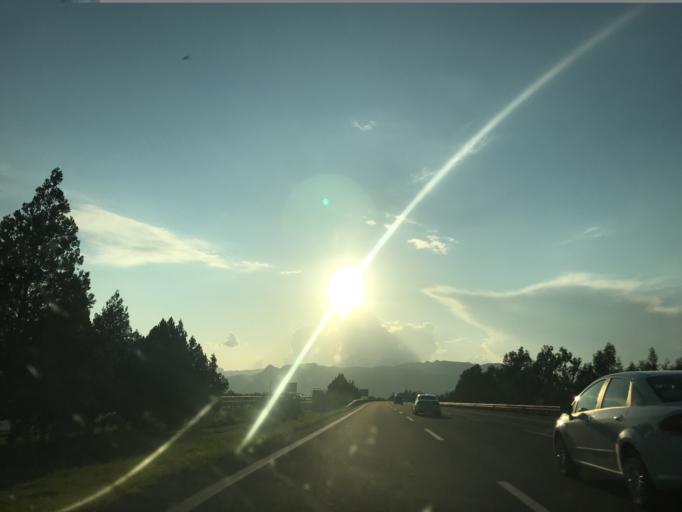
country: TR
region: Adana
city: Ceyhan
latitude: 36.9837
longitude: 35.7957
